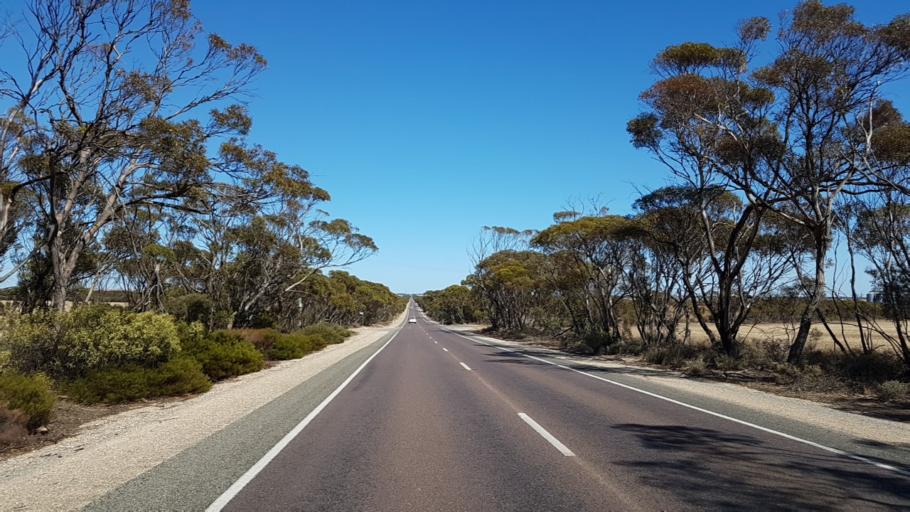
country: AU
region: South Australia
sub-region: Copper Coast
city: Kadina
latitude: -34.0526
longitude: 137.9927
